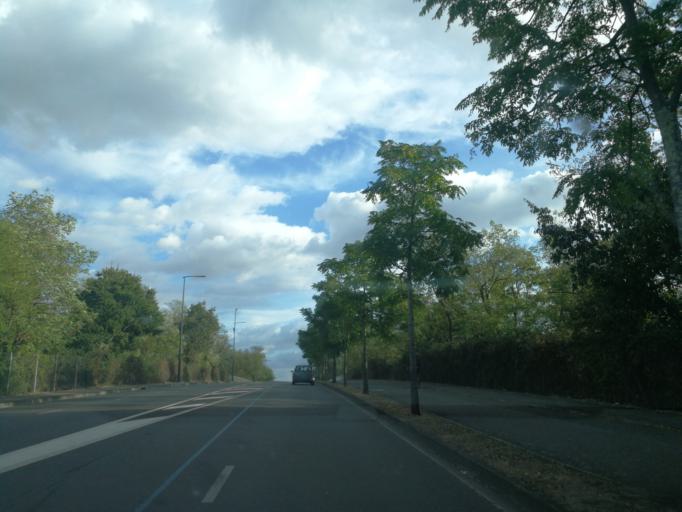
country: FR
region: Midi-Pyrenees
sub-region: Departement de la Haute-Garonne
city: L'Union
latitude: 43.6345
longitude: 1.4735
